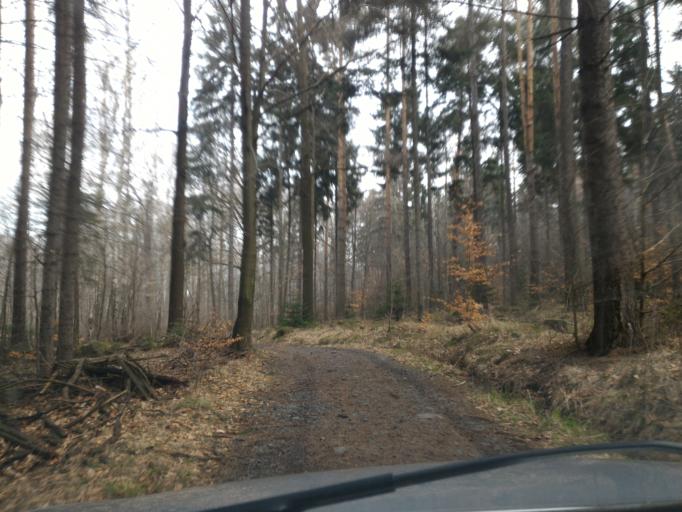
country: DE
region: Saxony
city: Kurort Oybin
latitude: 50.8586
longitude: 14.7588
